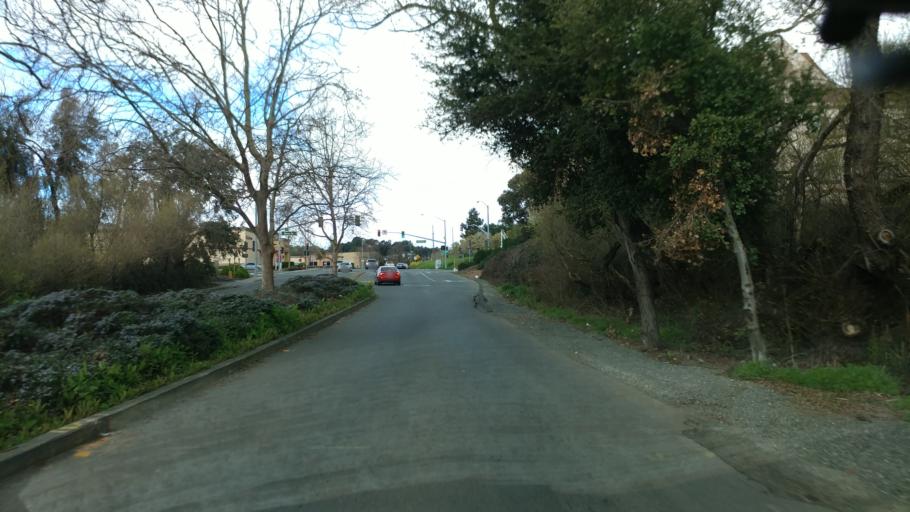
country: US
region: California
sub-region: Contra Costa County
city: Crockett
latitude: 38.0805
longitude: -122.1911
